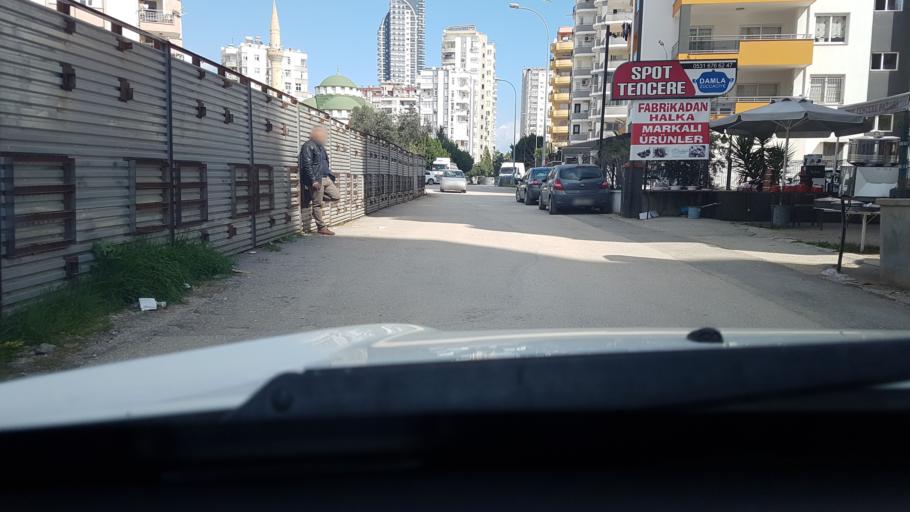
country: TR
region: Adana
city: Adana
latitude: 37.0434
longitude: 35.3025
